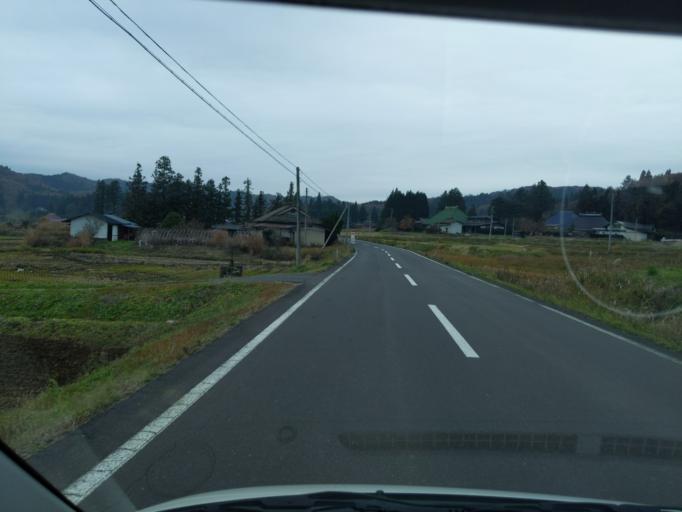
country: JP
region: Iwate
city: Kitakami
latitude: 39.2602
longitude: 141.1983
